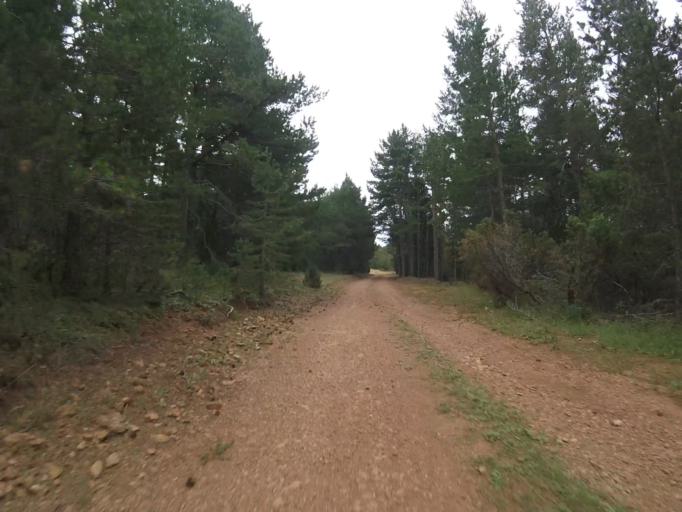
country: ES
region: Aragon
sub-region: Provincia de Teruel
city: Valdelinares
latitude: 40.3659
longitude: -0.6179
